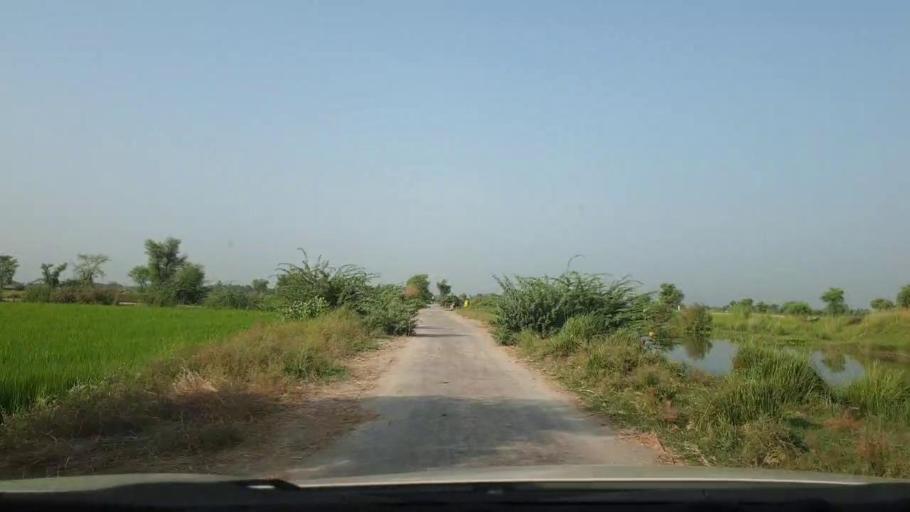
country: PK
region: Sindh
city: Larkana
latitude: 27.4941
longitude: 68.1695
